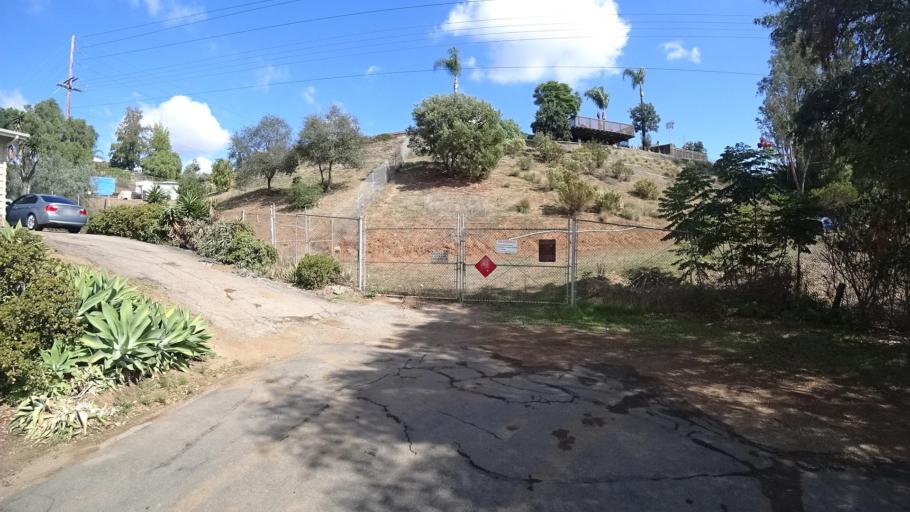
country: US
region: California
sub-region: San Diego County
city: Casa de Oro-Mount Helix
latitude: 32.7398
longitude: -116.9622
